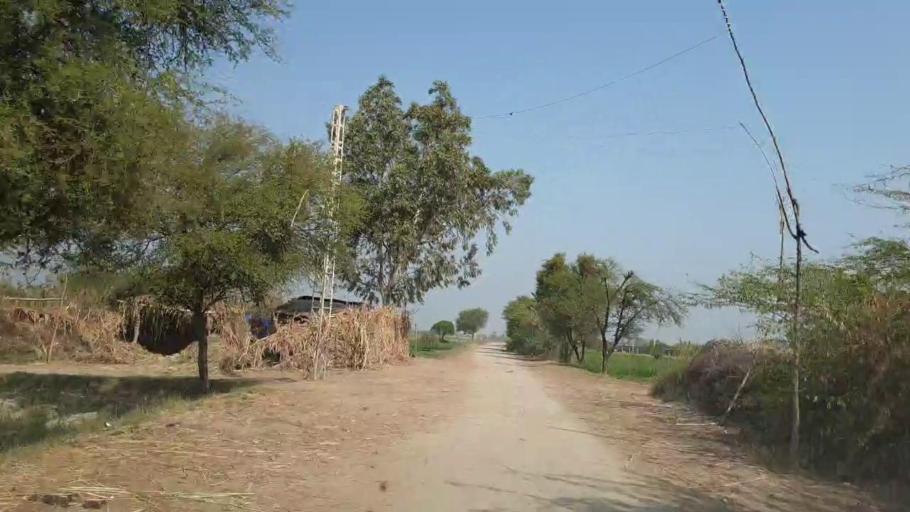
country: PK
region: Sindh
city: Mirpur Khas
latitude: 25.5899
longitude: 69.0149
